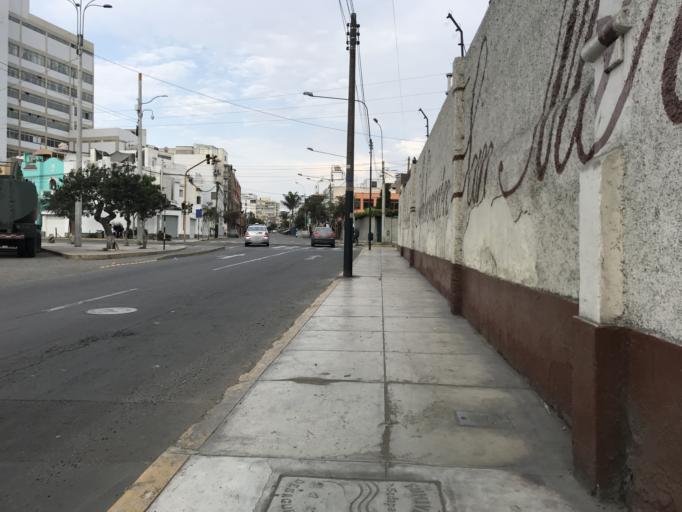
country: PE
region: Lima
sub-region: Lima
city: San Isidro
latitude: -12.0831
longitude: -77.0424
